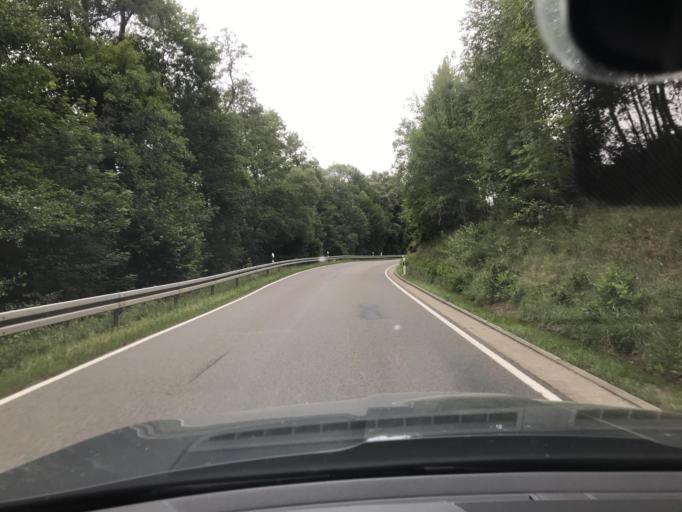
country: DE
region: Saxony-Anhalt
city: Harzgerode
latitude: 51.6404
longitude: 11.1048
